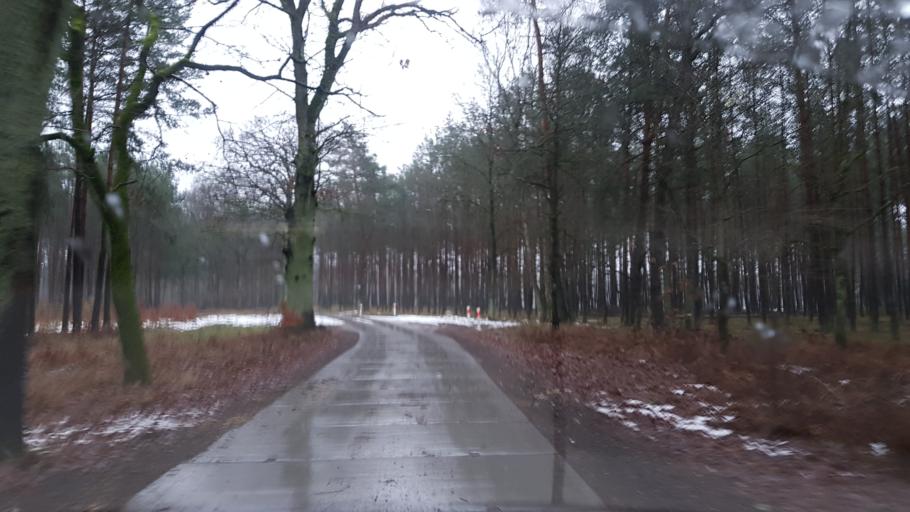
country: PL
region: West Pomeranian Voivodeship
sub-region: Powiat policki
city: Dobra
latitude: 53.5530
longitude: 14.4054
